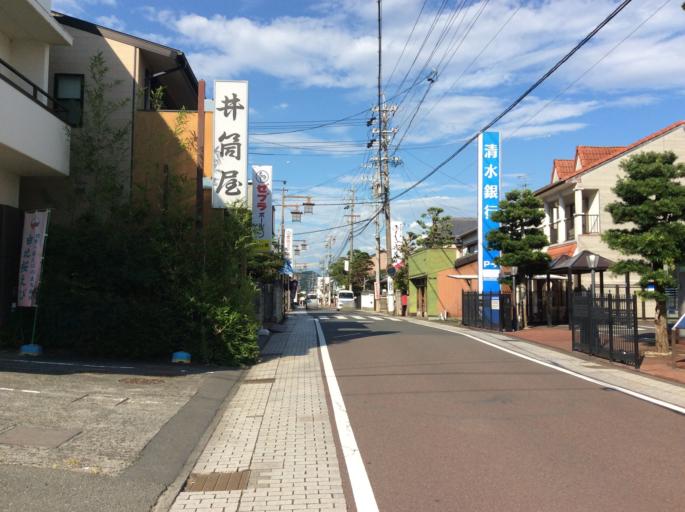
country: JP
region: Shizuoka
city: Fujinomiya
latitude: 35.1069
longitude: 138.5663
